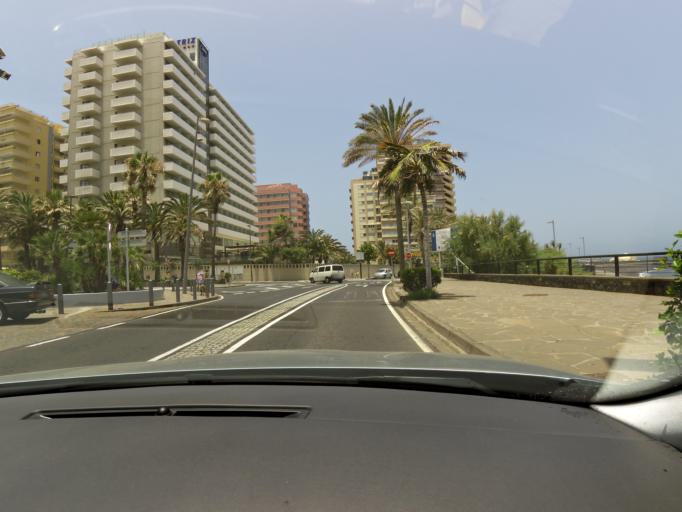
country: ES
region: Canary Islands
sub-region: Provincia de Santa Cruz de Tenerife
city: Puerto de la Cruz
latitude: 28.4171
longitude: -16.5414
